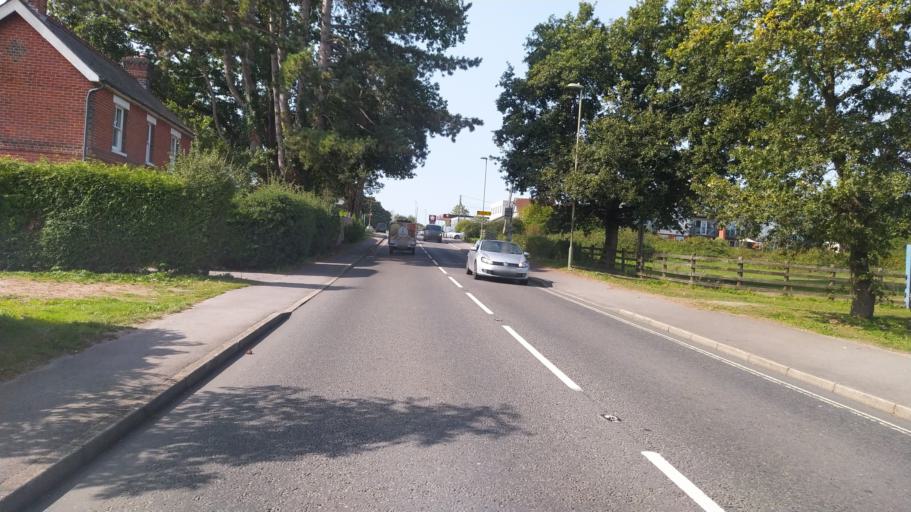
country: GB
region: England
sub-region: Hampshire
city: Hedge End
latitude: 50.9160
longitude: -1.2879
